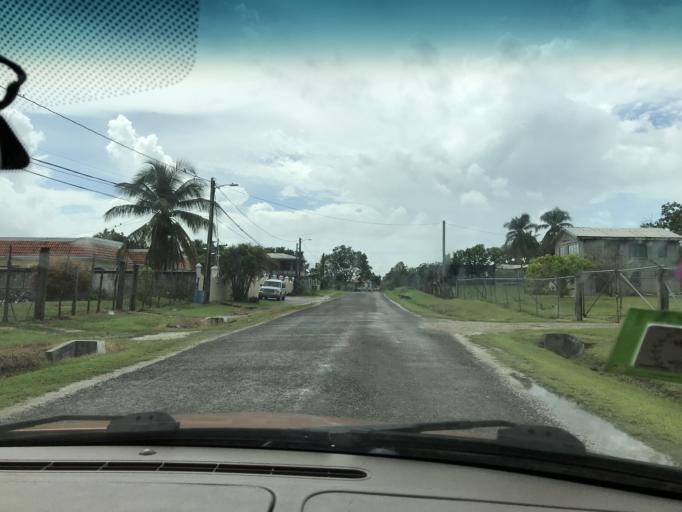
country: BZ
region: Orange Walk
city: Orange Walk
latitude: 18.0902
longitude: -88.5622
